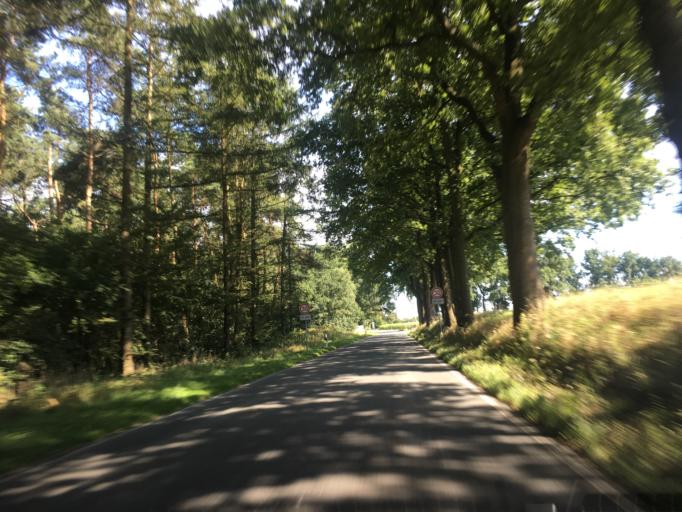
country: DE
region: North Rhine-Westphalia
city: Olfen
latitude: 51.7173
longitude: 7.3582
